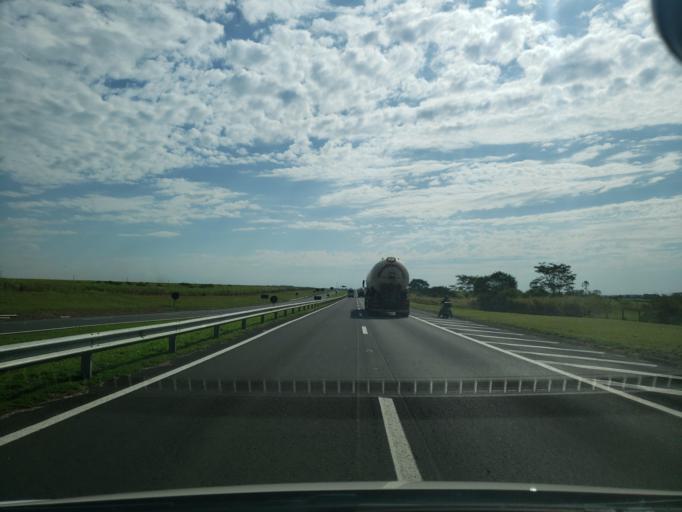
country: BR
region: Sao Paulo
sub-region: Promissao
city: Promissao
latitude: -21.6212
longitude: -49.8550
